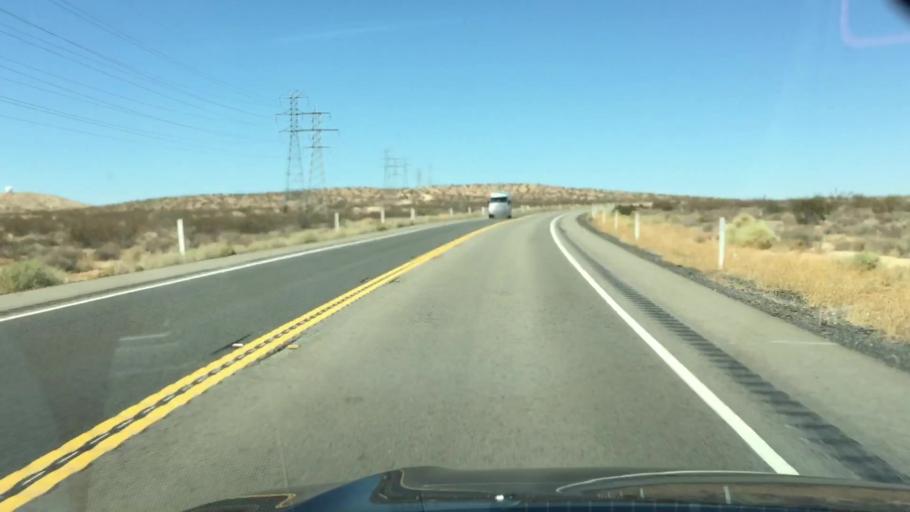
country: US
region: California
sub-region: Kern County
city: Boron
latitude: 35.0594
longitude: -117.5602
